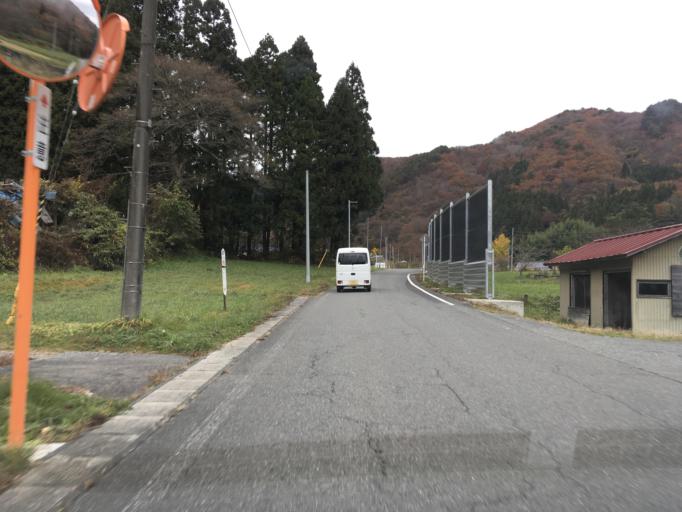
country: JP
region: Iwate
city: Mizusawa
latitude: 39.0941
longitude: 141.3459
